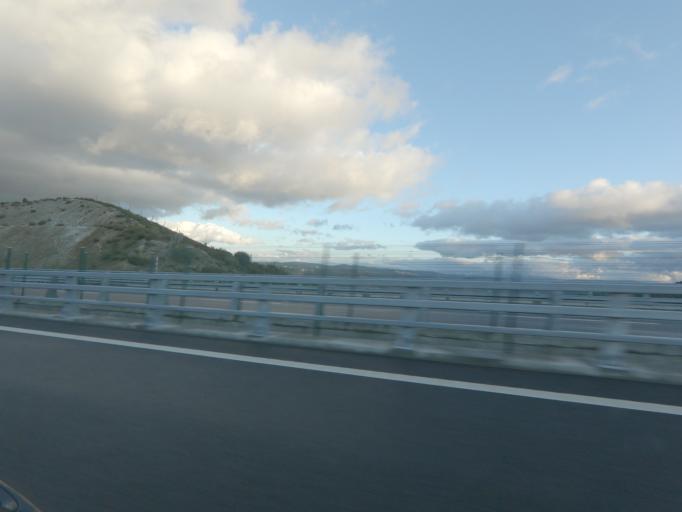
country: PT
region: Vila Real
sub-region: Vila Real
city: Vila Real
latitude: 41.2704
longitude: -7.7835
